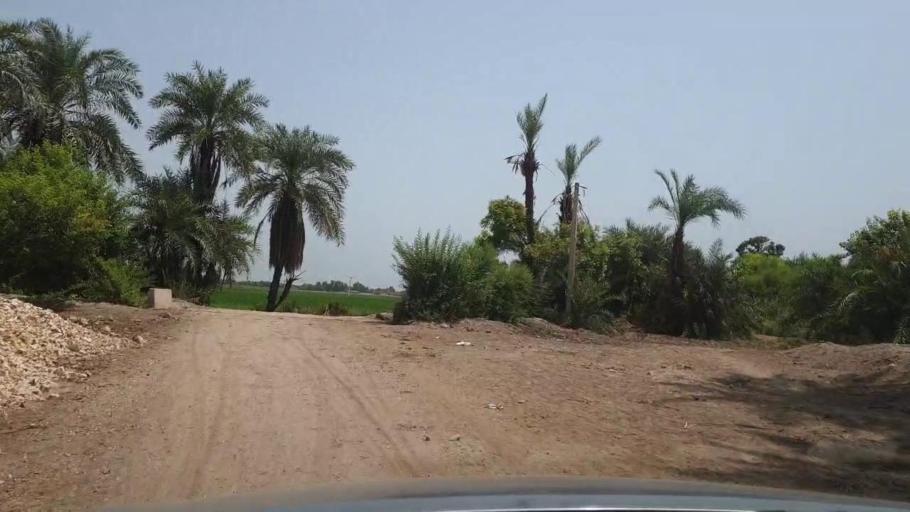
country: PK
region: Sindh
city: Ratodero
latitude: 27.7935
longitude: 68.3470
